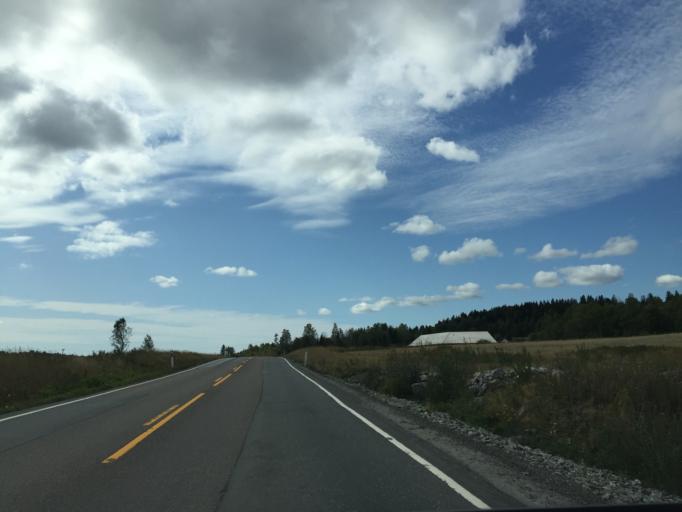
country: NO
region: Ostfold
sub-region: Hobol
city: Elvestad
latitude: 59.6177
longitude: 10.9411
